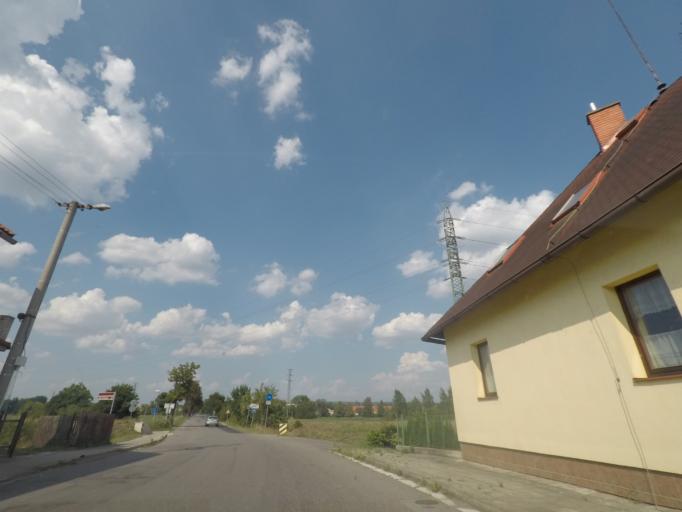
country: CZ
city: Albrechtice nad Orlici
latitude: 50.1452
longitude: 16.0648
